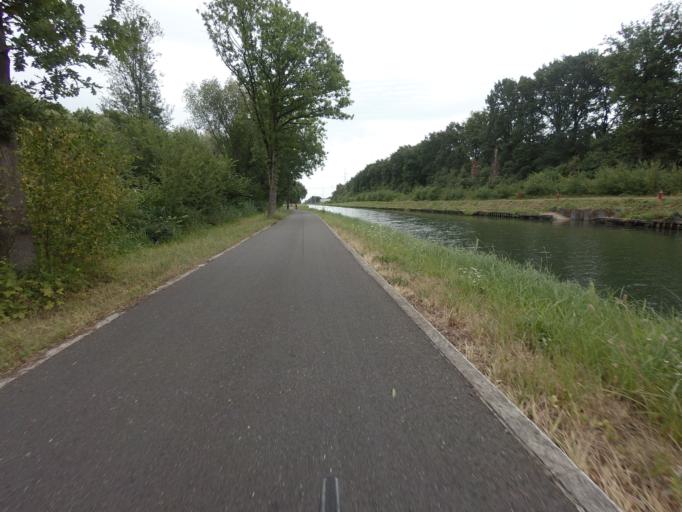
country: BE
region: Flanders
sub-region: Provincie Antwerpen
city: Brecht
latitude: 51.3165
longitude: 4.6046
